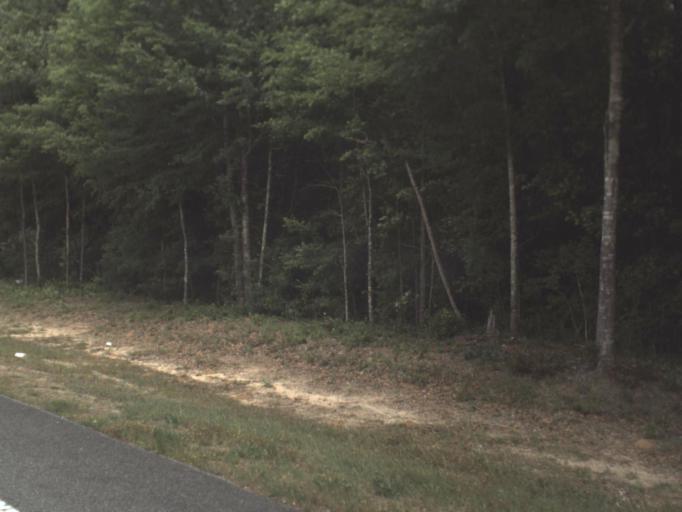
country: US
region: Florida
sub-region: Santa Rosa County
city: Point Baker
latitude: 30.7246
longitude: -87.0796
